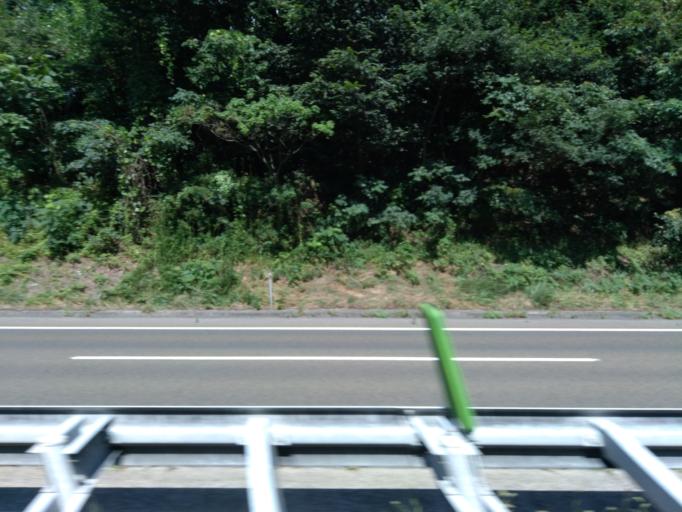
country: JP
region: Miyagi
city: Tomiya
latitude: 38.3913
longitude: 140.9003
